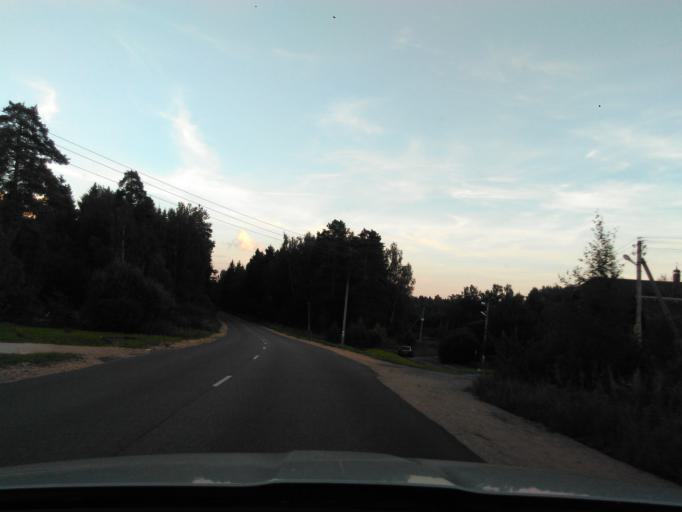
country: RU
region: Moskovskaya
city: Klin
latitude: 56.2414
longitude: 36.8317
